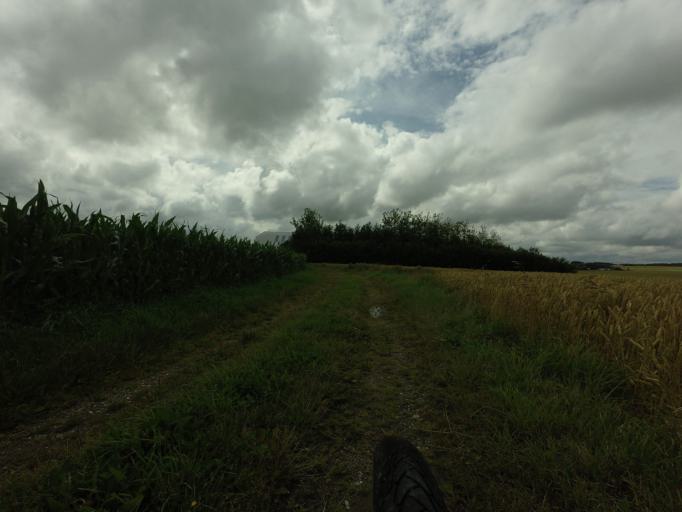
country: DK
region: North Denmark
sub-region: Jammerbugt Kommune
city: Pandrup
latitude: 57.2938
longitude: 9.7408
